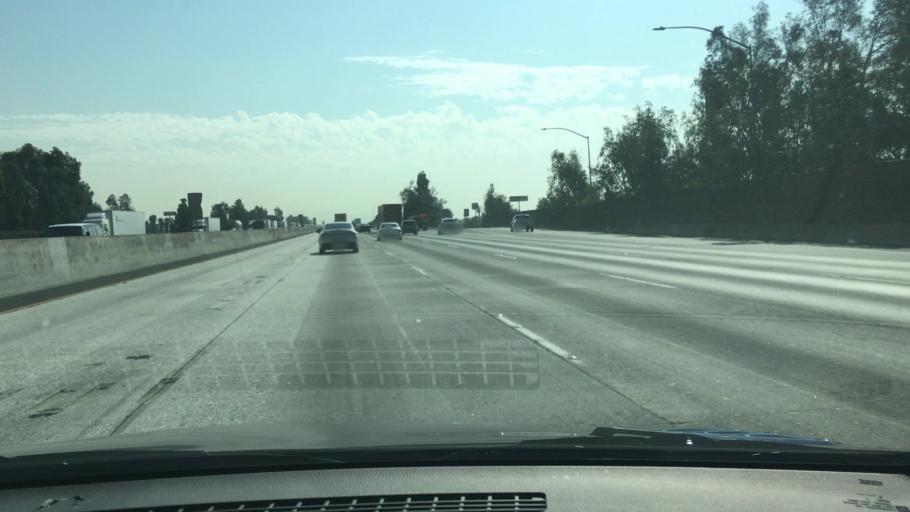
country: US
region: California
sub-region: San Bernardino County
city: Ontario
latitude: 34.0304
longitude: -117.6558
